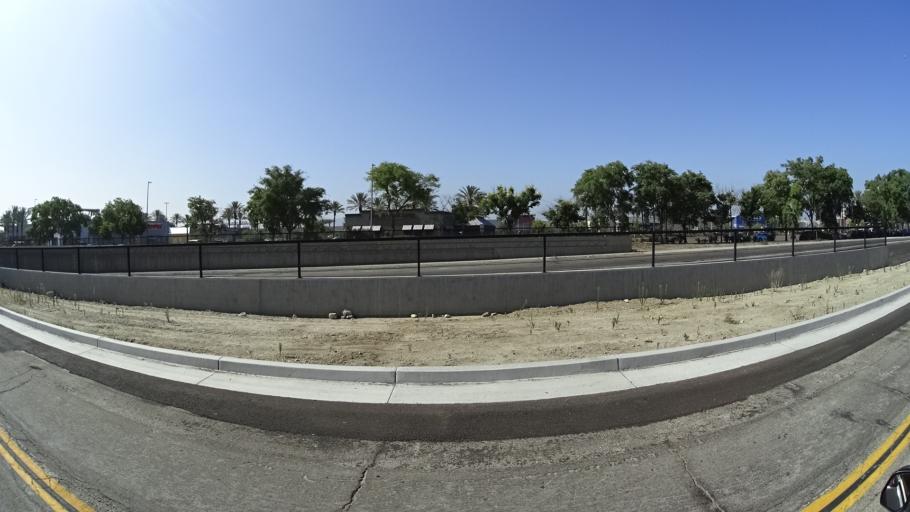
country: US
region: California
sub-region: Los Angeles County
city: Burbank
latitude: 34.1918
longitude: -118.3305
